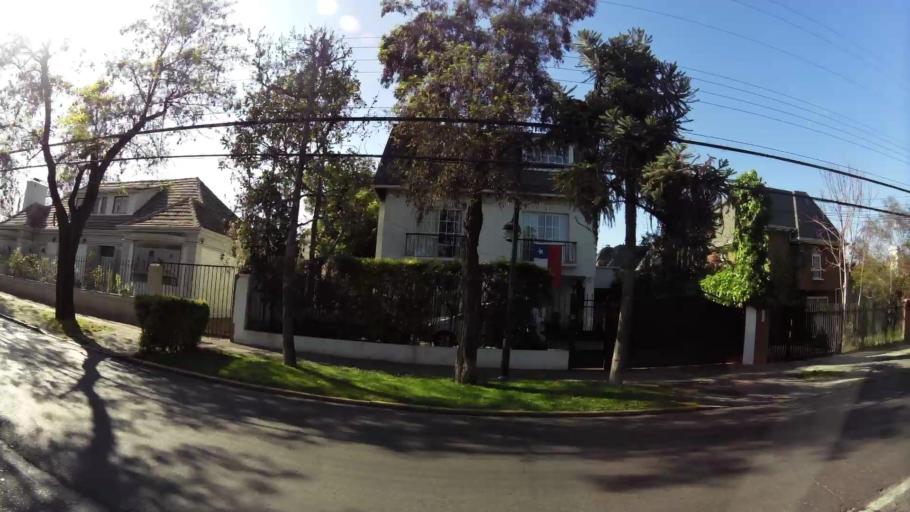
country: CL
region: Santiago Metropolitan
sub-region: Provincia de Santiago
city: Villa Presidente Frei, Nunoa, Santiago, Chile
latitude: -33.4377
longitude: -70.5857
